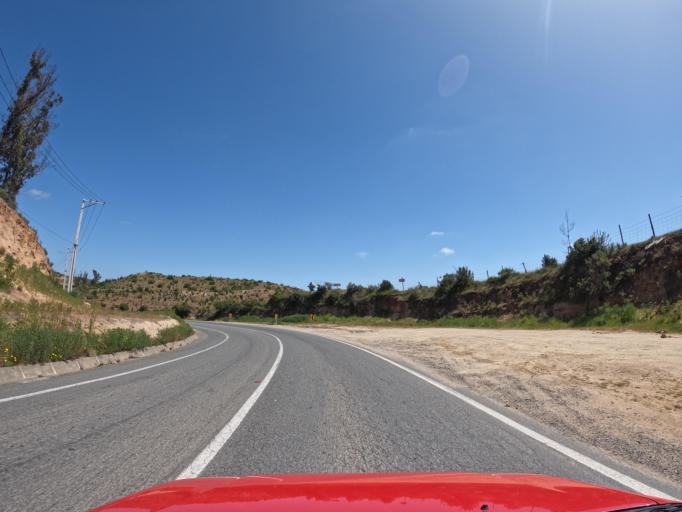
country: CL
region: O'Higgins
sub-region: Provincia de Colchagua
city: Santa Cruz
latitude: -34.6612
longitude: -71.8435
